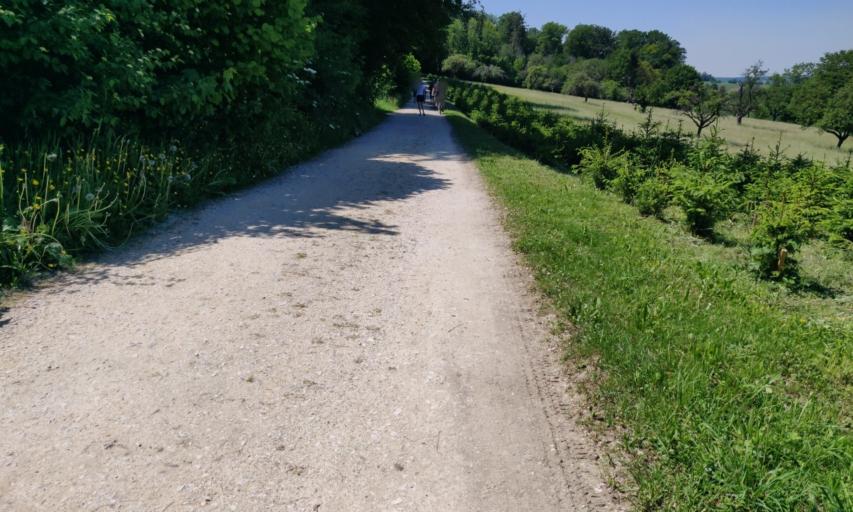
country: CH
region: Basel-Landschaft
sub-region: Bezirk Arlesheim
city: Pfeffingen
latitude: 47.4705
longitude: 7.5759
